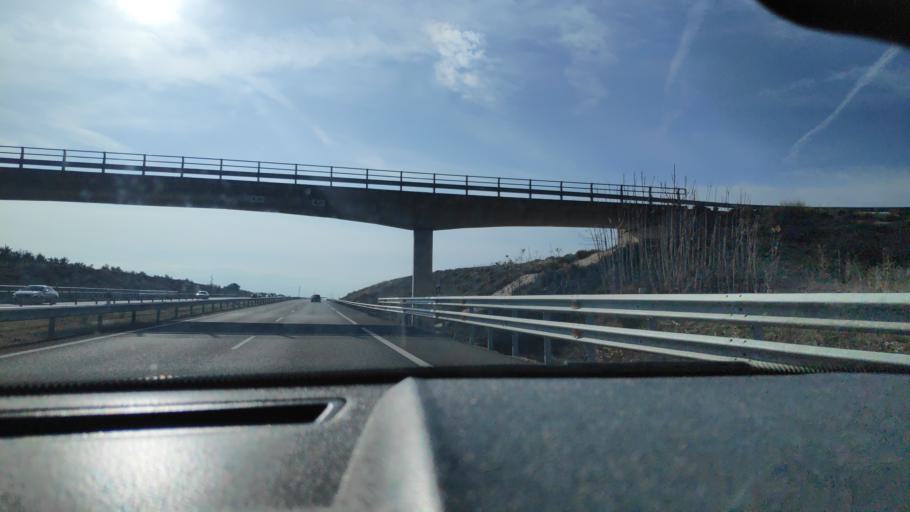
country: ES
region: Andalusia
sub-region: Provincia de Jaen
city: Jaen
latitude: 37.8499
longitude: -3.7647
